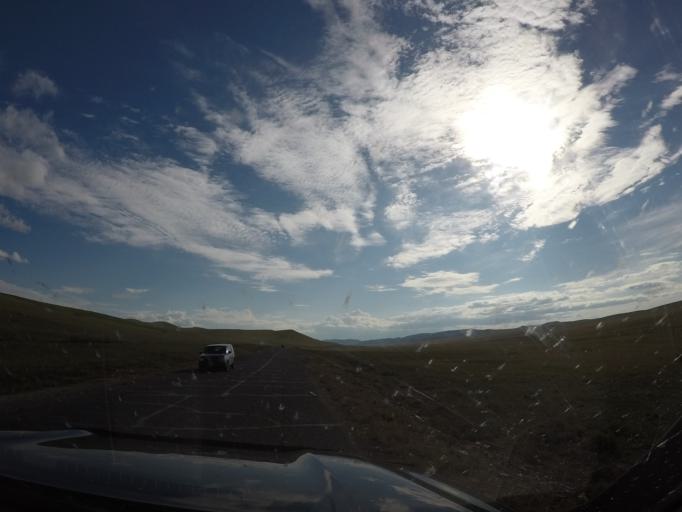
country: MN
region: Hentiy
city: Modot
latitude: 47.7725
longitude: 108.6536
